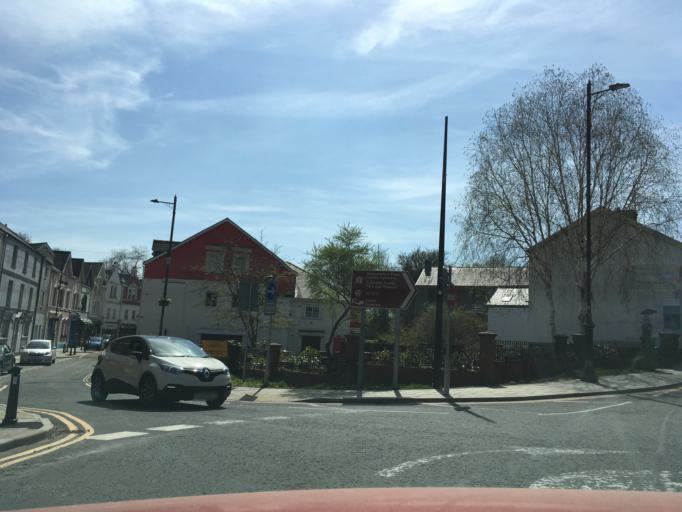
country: GB
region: Wales
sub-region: Merthyr Tydfil County Borough
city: Merthyr Tydfil
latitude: 51.7500
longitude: -3.3768
